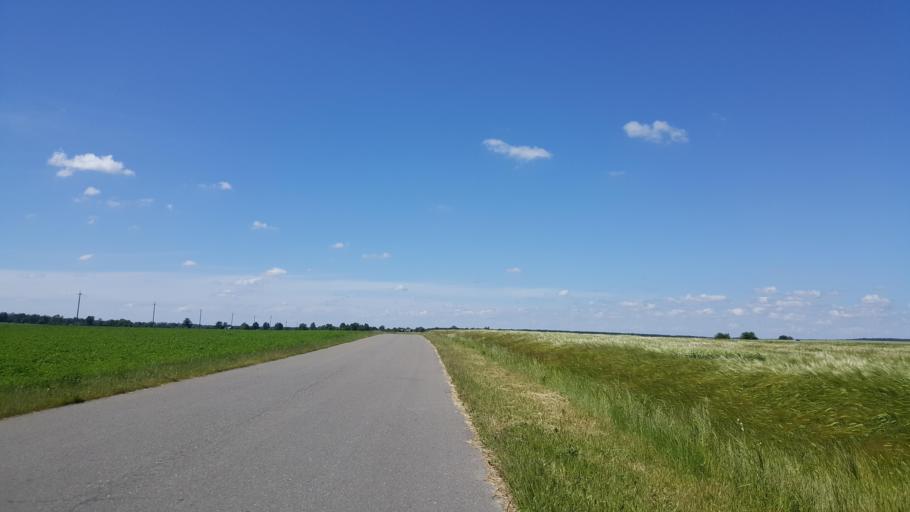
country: BY
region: Brest
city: Kamyanyets
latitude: 52.3827
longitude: 23.7932
